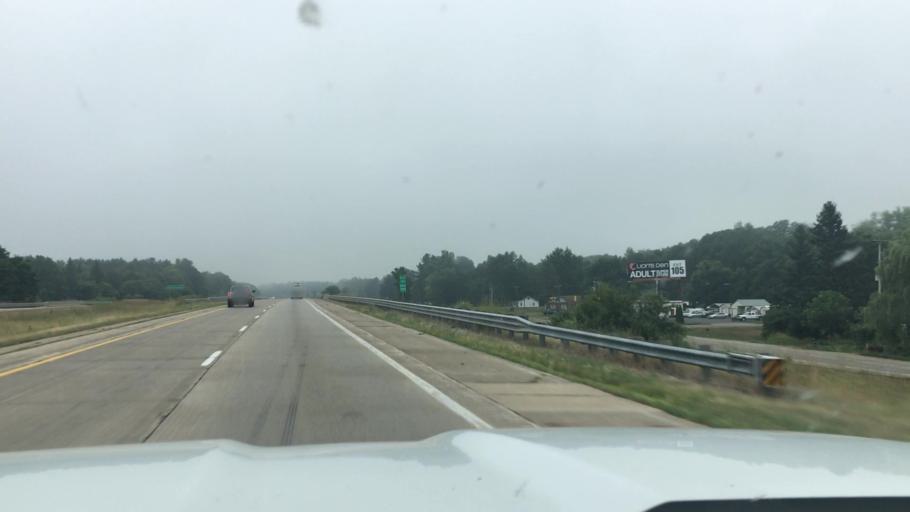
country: US
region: Michigan
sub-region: Shiawassee County
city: Perry
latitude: 42.8129
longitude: -84.2955
